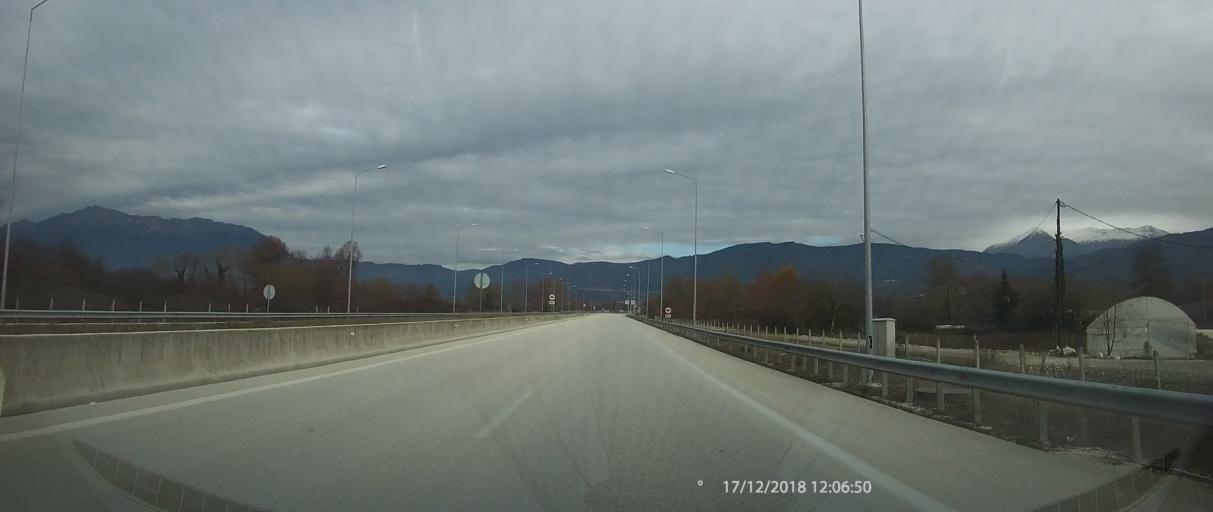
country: GR
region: Epirus
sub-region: Nomos Ioanninon
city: Koutselio
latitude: 39.6126
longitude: 20.9422
